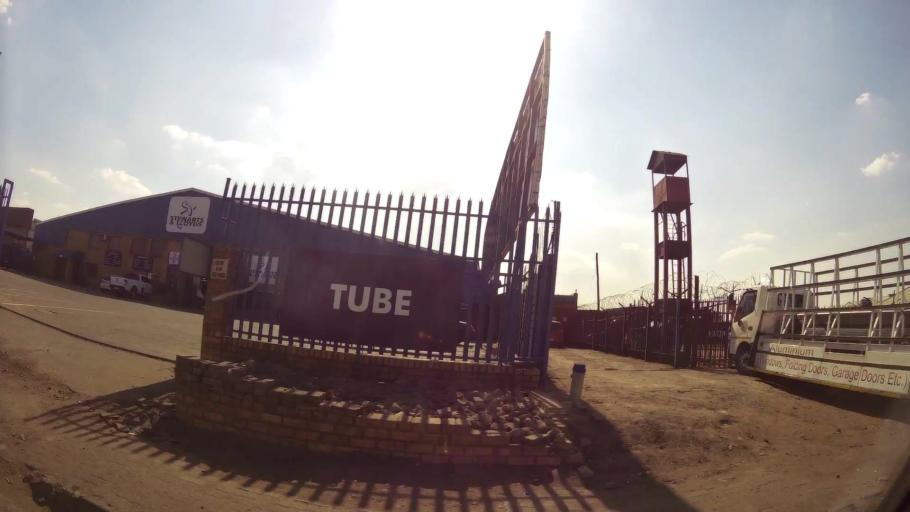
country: ZA
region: Gauteng
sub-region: Ekurhuleni Metropolitan Municipality
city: Boksburg
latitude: -26.2086
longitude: 28.2684
